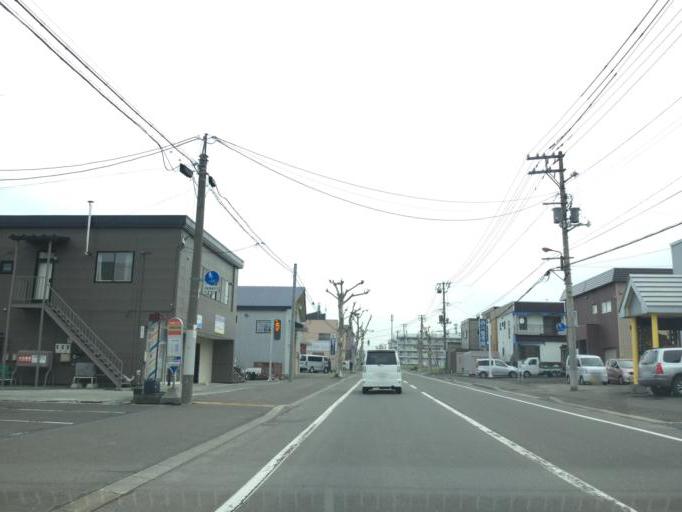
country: JP
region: Hokkaido
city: Iwamizawa
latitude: 43.2070
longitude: 141.7777
